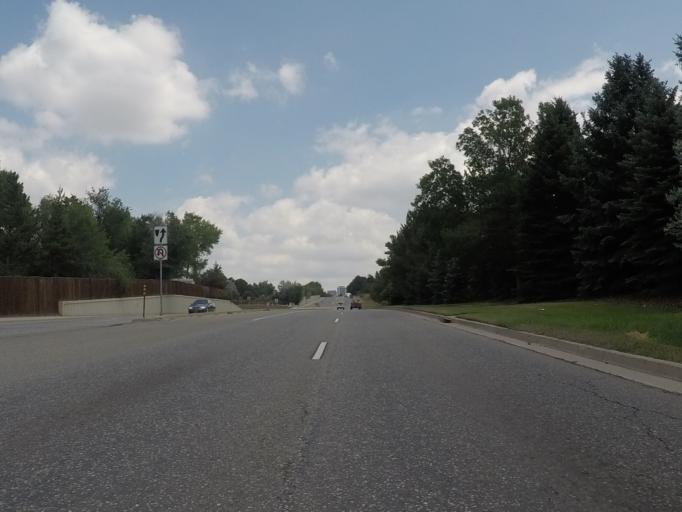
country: US
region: Colorado
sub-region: Arapahoe County
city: Greenwood Village
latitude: 39.6240
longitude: -104.9370
